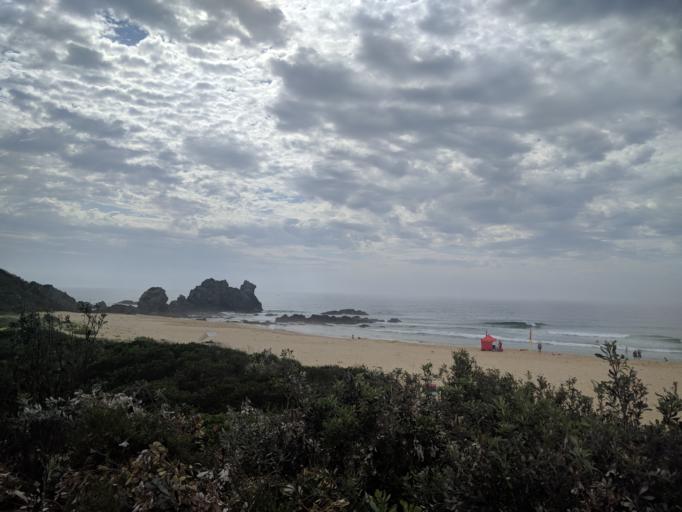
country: AU
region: New South Wales
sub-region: Bega Valley
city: Bermagui
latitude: -36.4266
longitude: 150.0795
